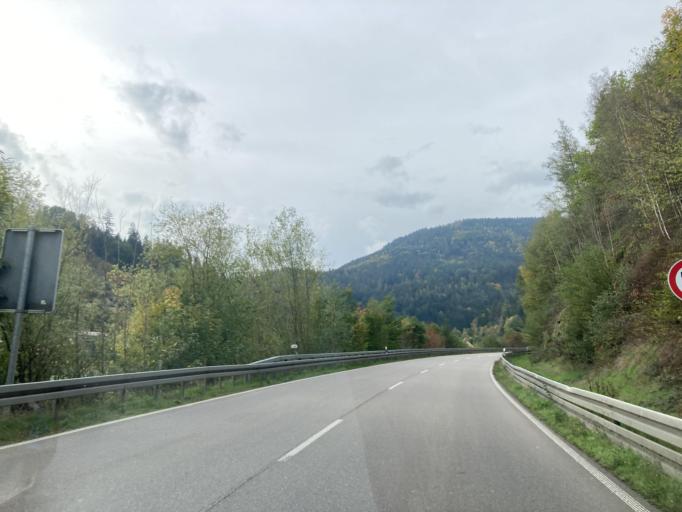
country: DE
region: Baden-Wuerttemberg
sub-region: Karlsruhe Region
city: Forbach
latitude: 48.6735
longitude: 8.3547
